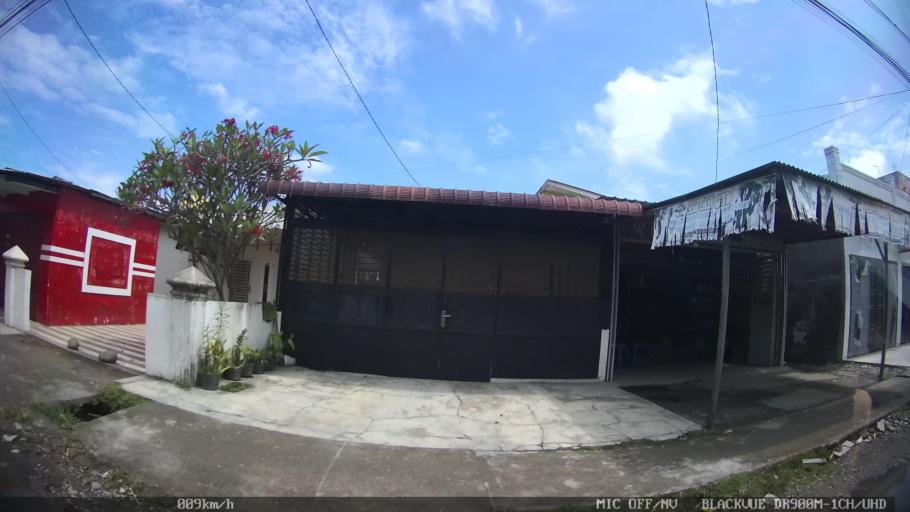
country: ID
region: North Sumatra
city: Medan
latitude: 3.5910
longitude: 98.7529
